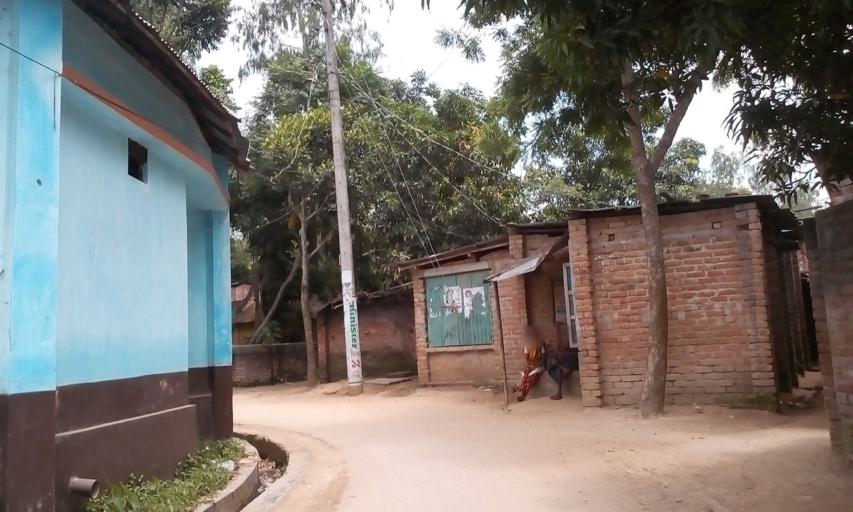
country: IN
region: West Bengal
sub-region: Dakshin Dinajpur
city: Balurghat
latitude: 25.3874
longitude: 88.9944
